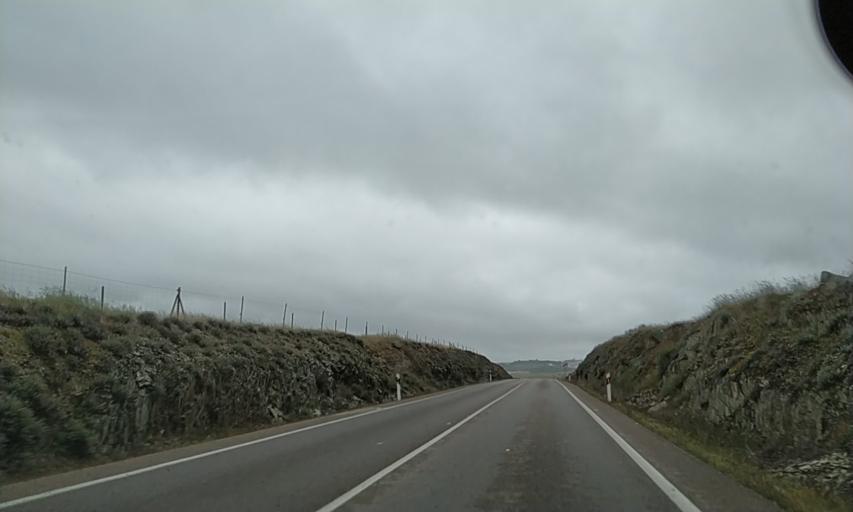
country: ES
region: Extremadura
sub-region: Provincia de Caceres
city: Caceres
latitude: 39.5142
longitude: -6.3957
